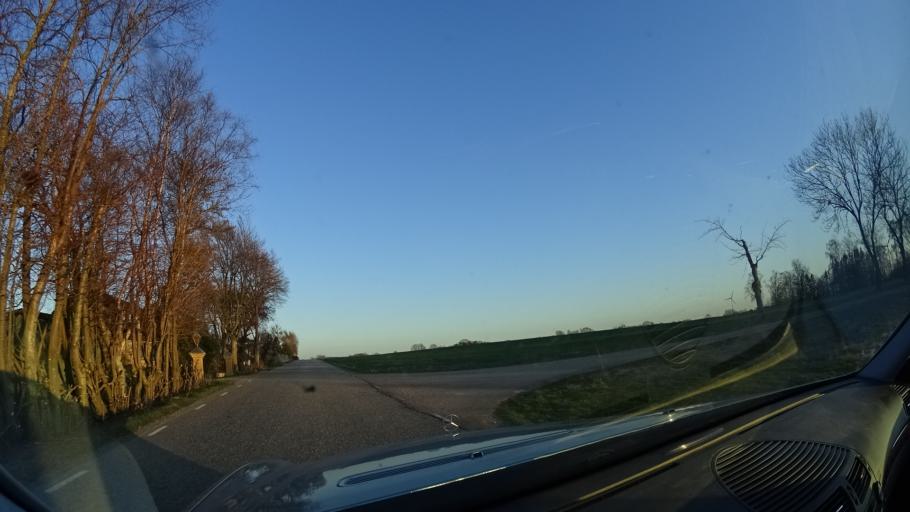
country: SE
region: Skane
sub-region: Hoors Kommun
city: Loberod
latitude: 55.8448
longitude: 13.4502
